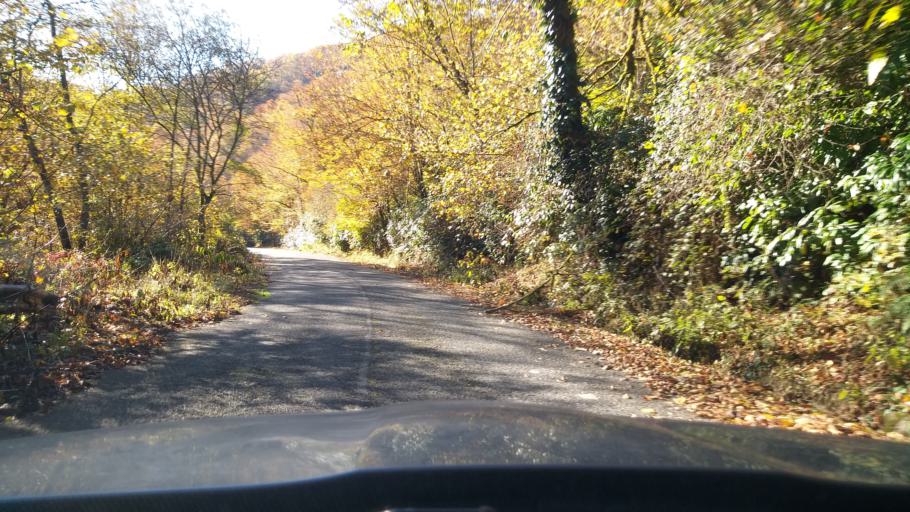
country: GE
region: Abkhazia
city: Bich'vinta
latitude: 43.1901
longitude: 40.4544
